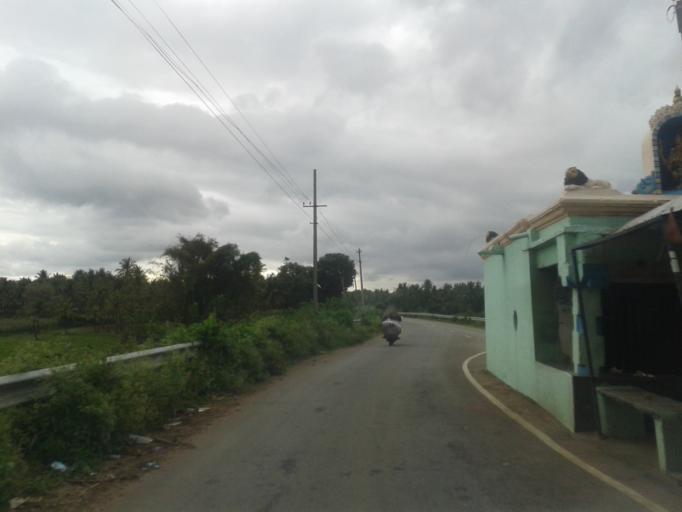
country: IN
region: Karnataka
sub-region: Hassan
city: Channarayapatna
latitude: 12.8814
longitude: 76.4207
